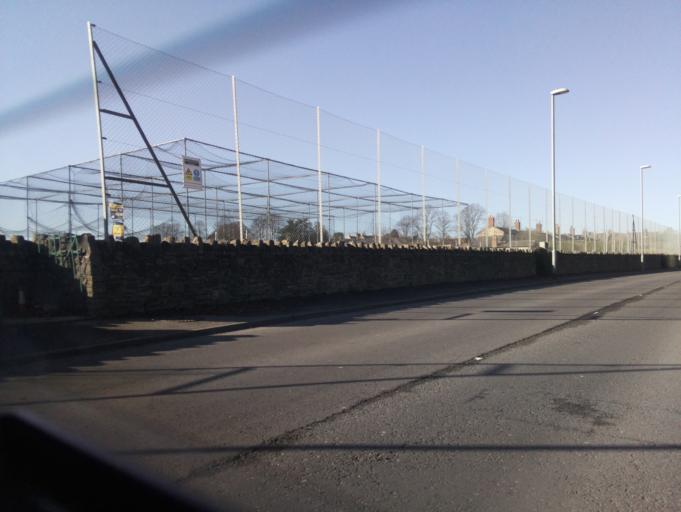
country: GB
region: England
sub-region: Dorset
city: Sherborne
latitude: 50.9424
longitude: -2.5222
